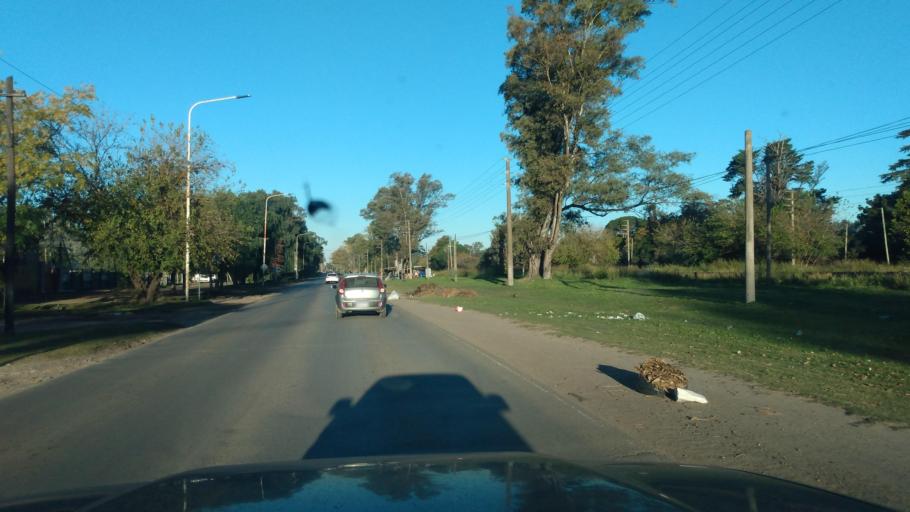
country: AR
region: Buenos Aires
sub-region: Partido de General Rodriguez
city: General Rodriguez
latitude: -34.6334
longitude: -58.8499
